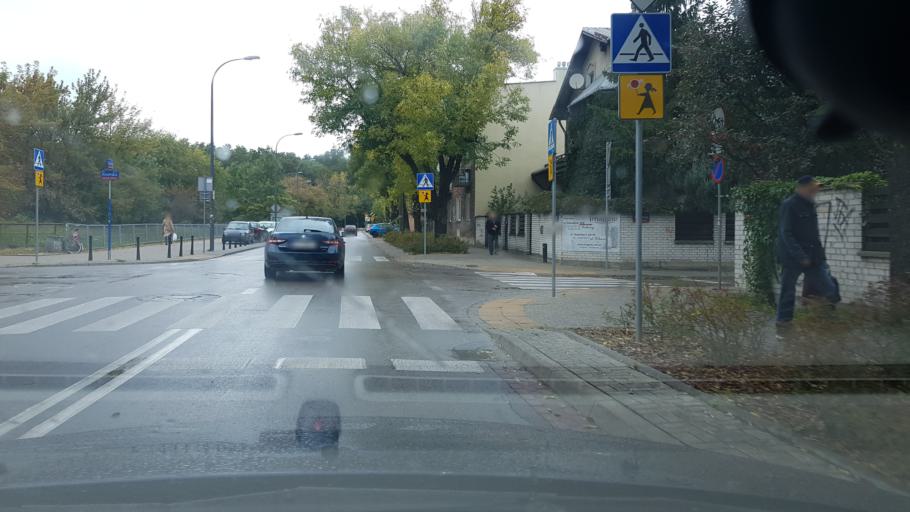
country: PL
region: Masovian Voivodeship
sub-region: Warszawa
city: Zoliborz
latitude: 52.2838
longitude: 20.9715
